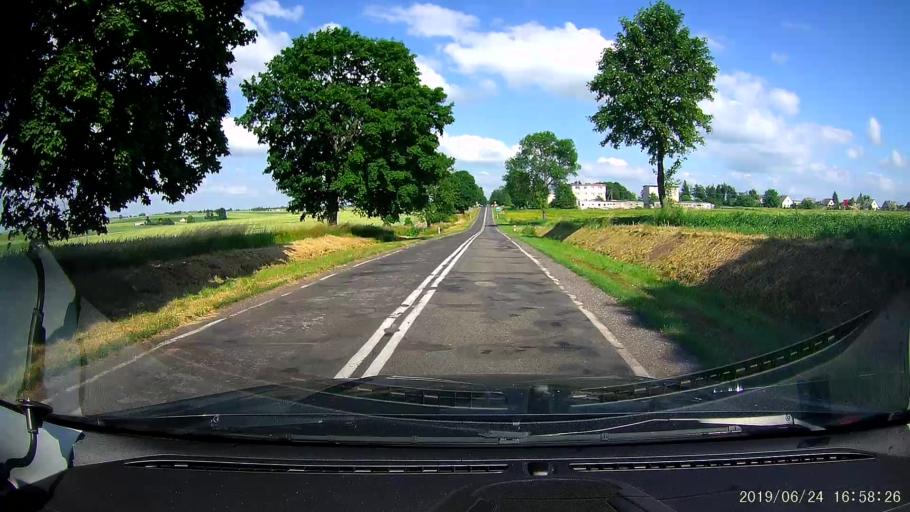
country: PL
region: Lublin Voivodeship
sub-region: Powiat tomaszowski
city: Telatyn
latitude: 50.5252
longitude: 23.8806
